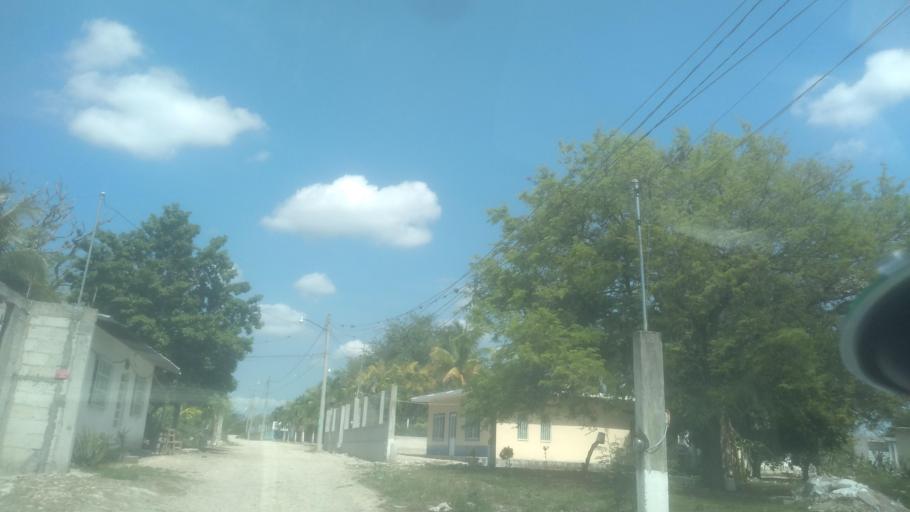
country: MX
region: Veracruz
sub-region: Emiliano Zapata
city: Plan del Rio
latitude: 19.3930
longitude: -96.6343
